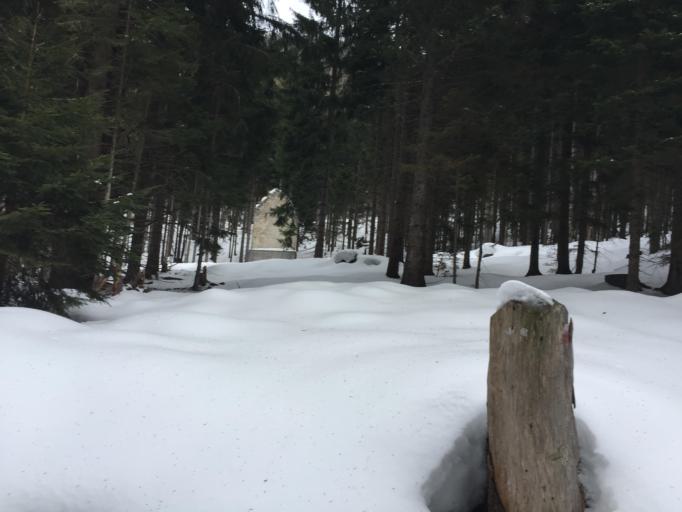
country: AT
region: Carinthia
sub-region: Politischer Bezirk Villach Land
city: Arnoldstein
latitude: 46.5136
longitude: 13.7007
